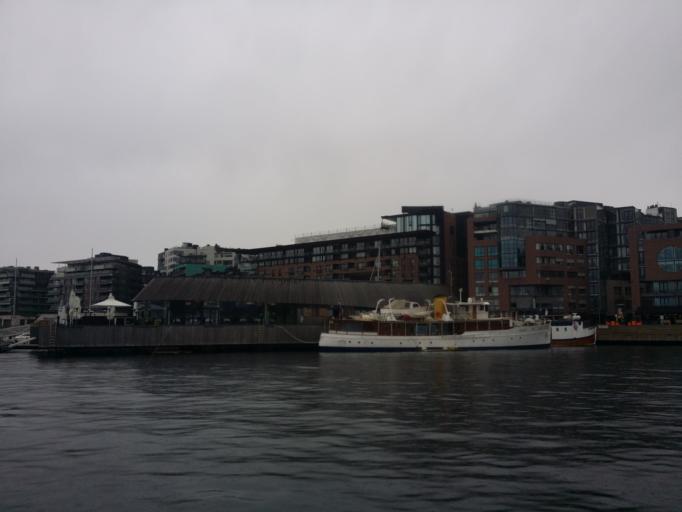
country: NO
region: Oslo
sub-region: Oslo
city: Oslo
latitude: 59.9084
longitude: 10.7275
